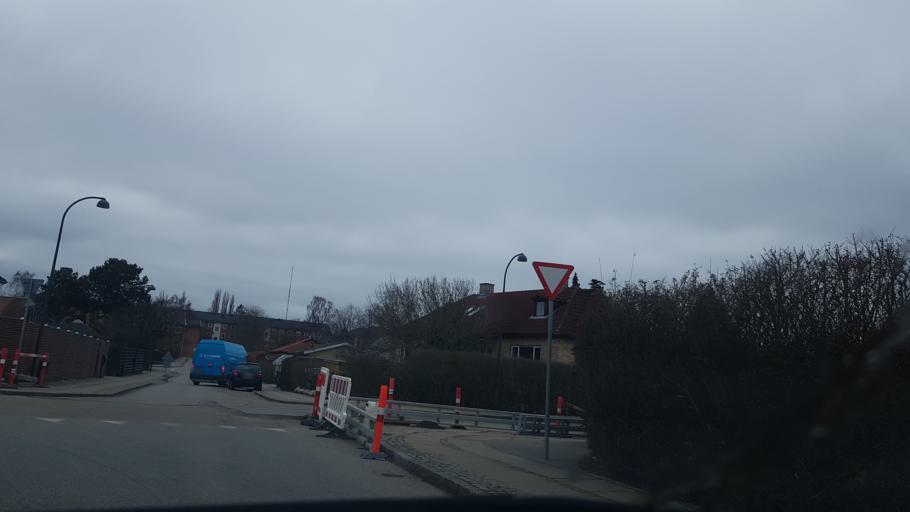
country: DK
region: Capital Region
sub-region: Gladsaxe Municipality
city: Buddinge
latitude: 55.7487
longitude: 12.5018
